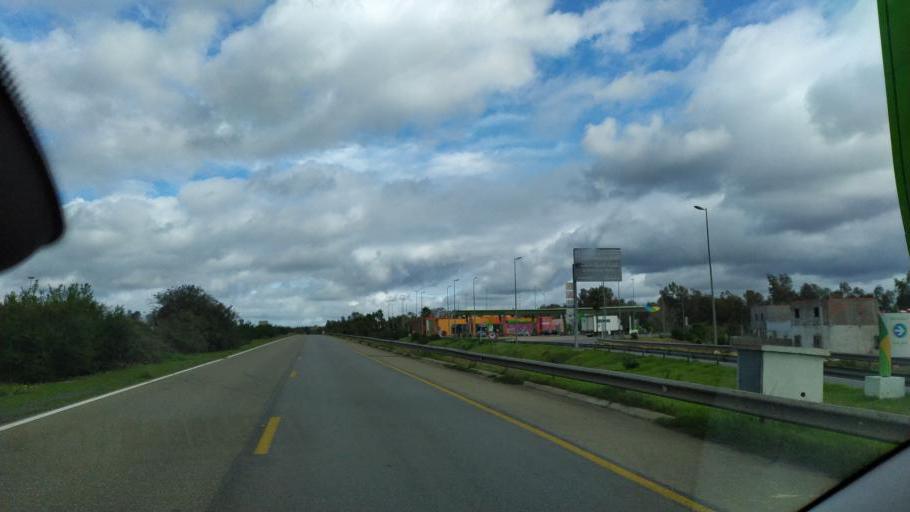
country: MA
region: Gharb-Chrarda-Beni Hssen
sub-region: Kenitra Province
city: Lalla Mimouna
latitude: 34.8742
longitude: -6.2149
